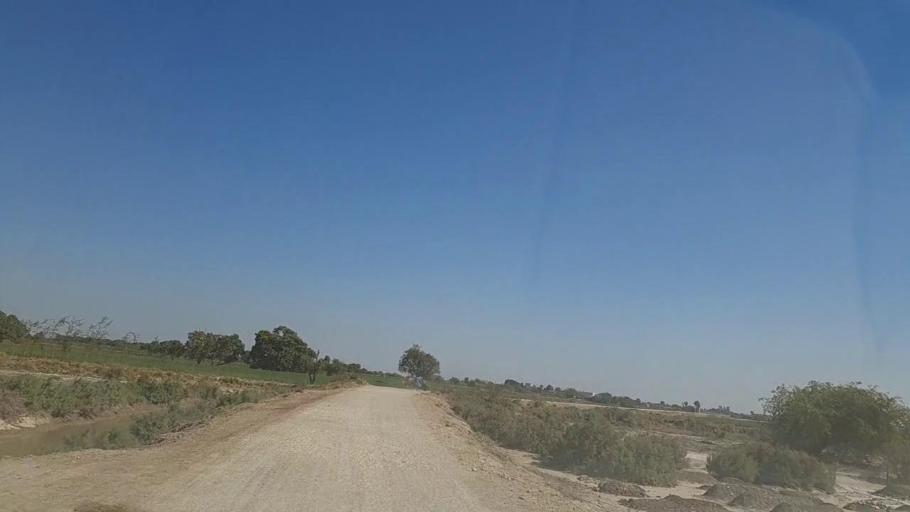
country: PK
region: Sindh
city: Digri
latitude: 25.1182
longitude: 69.1093
